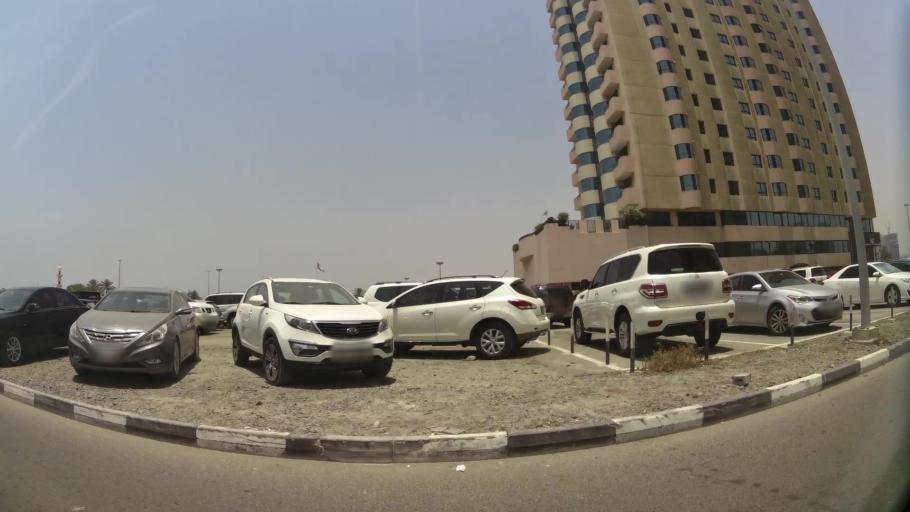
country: AE
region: Ash Shariqah
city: Sharjah
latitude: 25.3376
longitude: 55.3752
